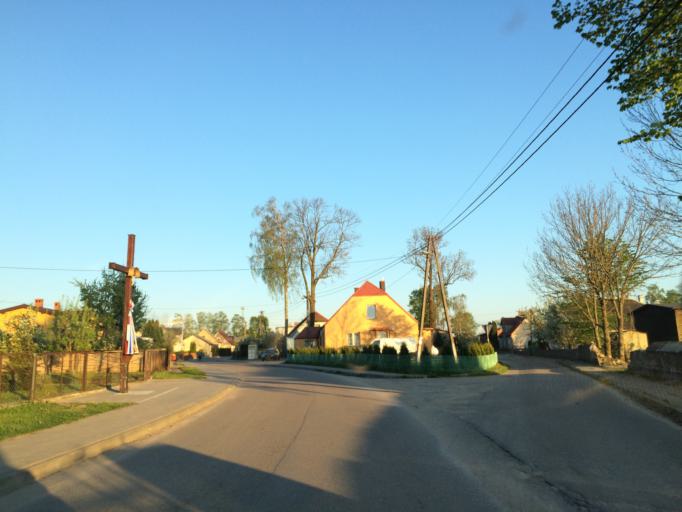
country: PL
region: Warmian-Masurian Voivodeship
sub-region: Powiat ilawski
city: Lubawa
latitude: 53.4948
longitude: 19.8376
